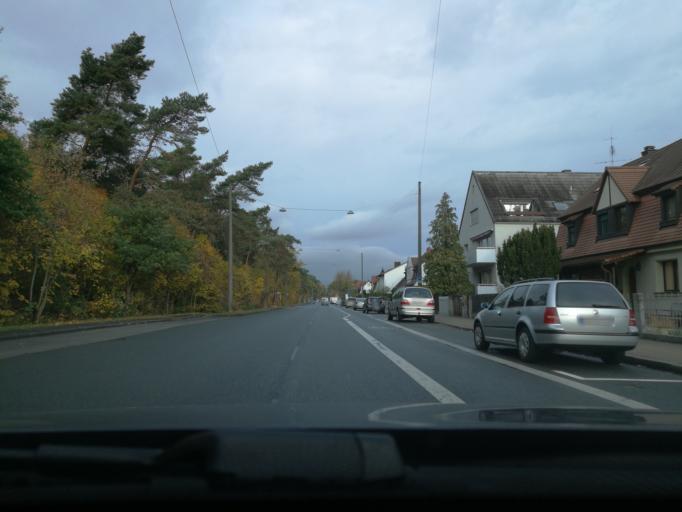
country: DE
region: Bavaria
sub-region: Regierungsbezirk Mittelfranken
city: Furth
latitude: 49.4896
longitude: 10.9927
